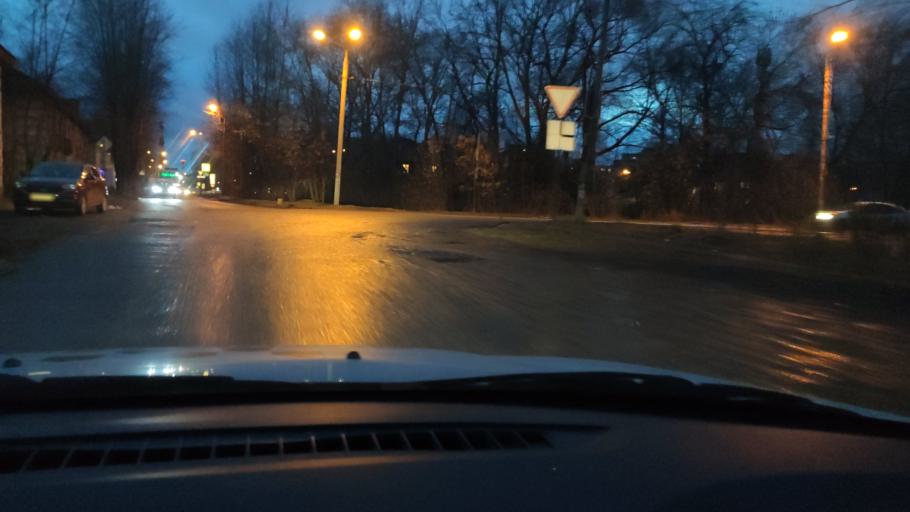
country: RU
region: Perm
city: Perm
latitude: 57.9746
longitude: 56.2785
